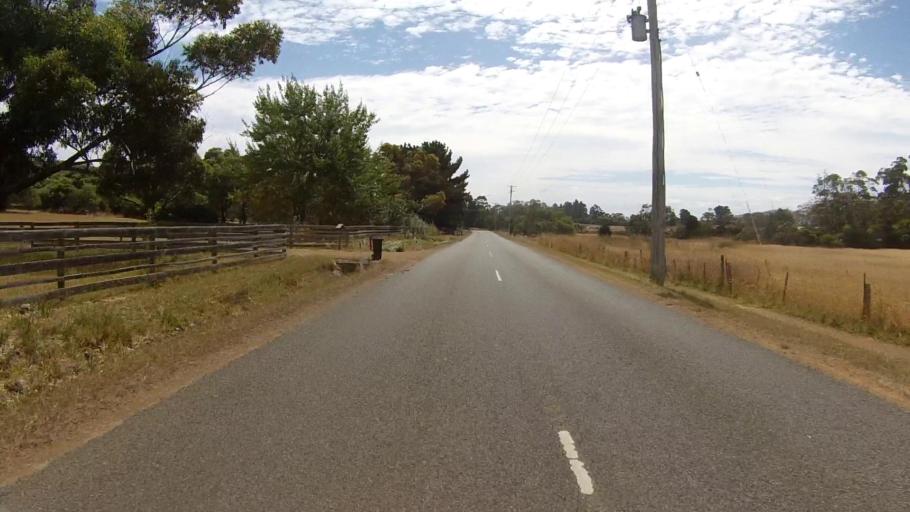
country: AU
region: Tasmania
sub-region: Clarence
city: Sandford
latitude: -42.9784
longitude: 147.5126
